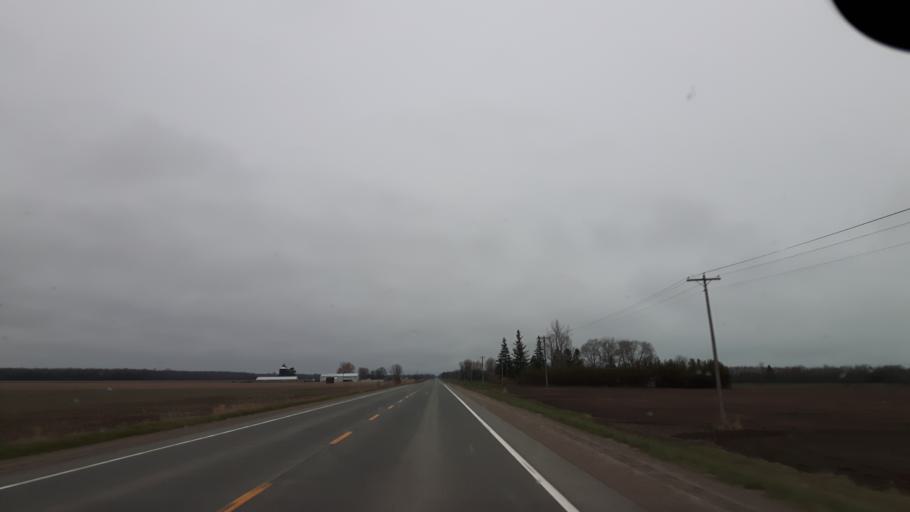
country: CA
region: Ontario
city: Goderich
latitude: 43.6381
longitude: -81.7057
